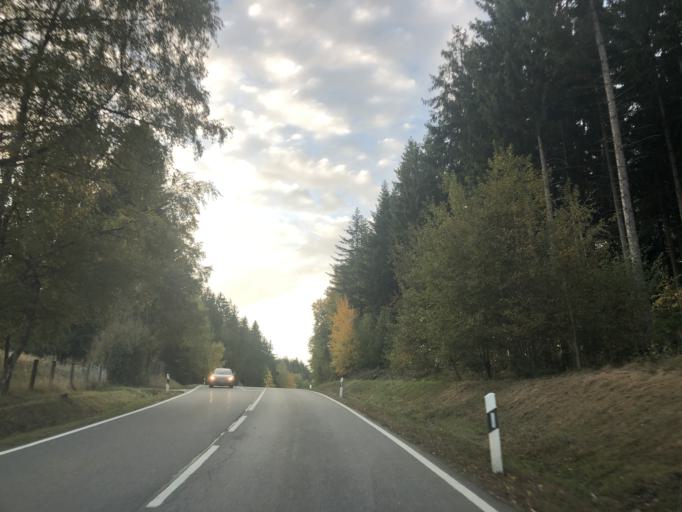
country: DE
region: Bavaria
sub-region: Lower Bavaria
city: Langdorf
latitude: 49.0161
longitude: 13.1445
